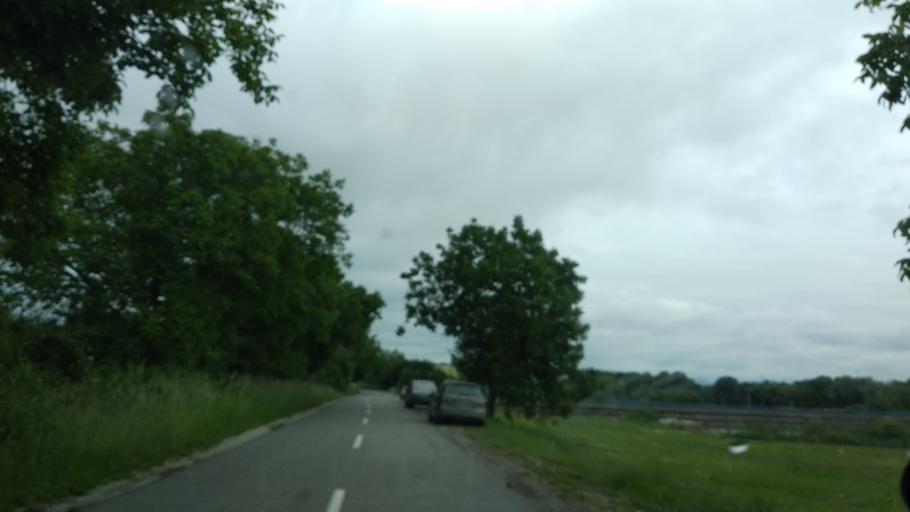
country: SK
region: Nitriansky
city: Trencianske Teplice
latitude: 48.7903
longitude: 18.1365
